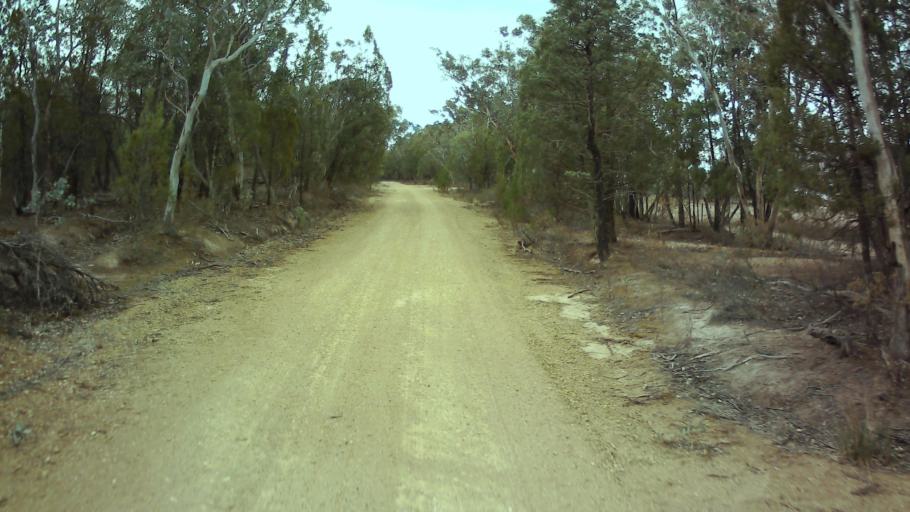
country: AU
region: New South Wales
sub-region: Weddin
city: Grenfell
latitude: -33.8844
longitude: 148.1579
